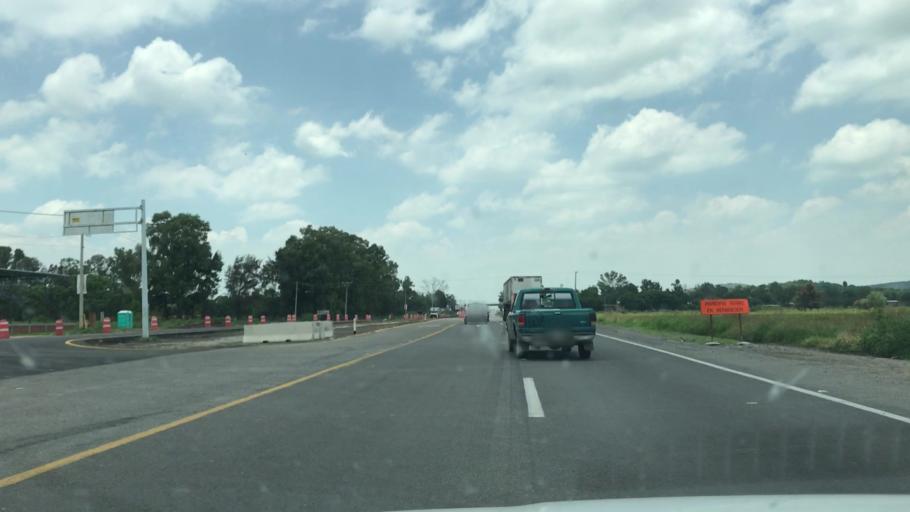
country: MX
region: Guanajuato
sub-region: Irapuato
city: San Ignacio de Rivera (Ojo de Agua)
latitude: 20.5328
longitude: -101.4594
